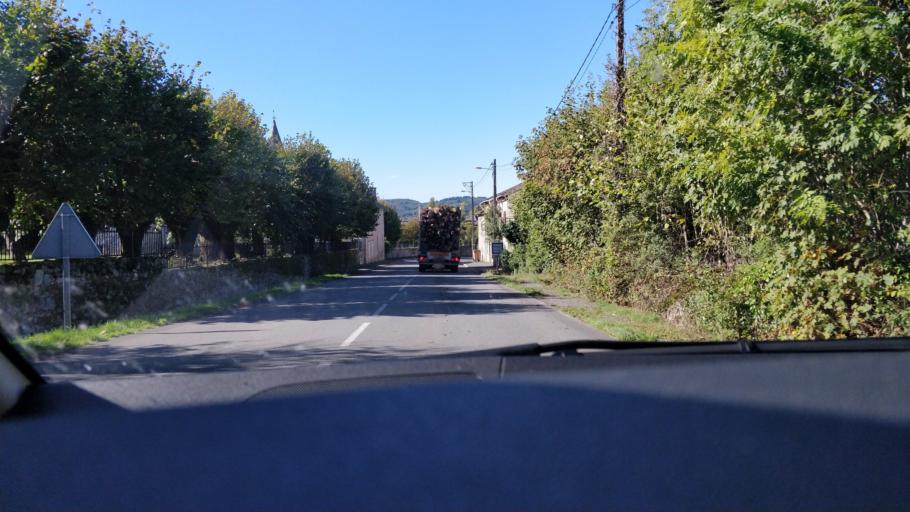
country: FR
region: Limousin
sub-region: Departement de la Haute-Vienne
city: Sauviat-sur-Vige
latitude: 45.9193
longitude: 1.6381
